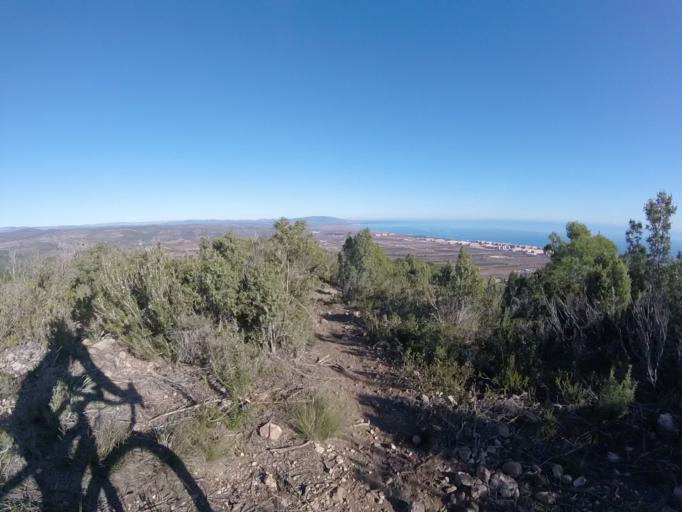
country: ES
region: Valencia
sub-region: Provincia de Castello
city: Orpesa/Oropesa del Mar
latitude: 40.1044
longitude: 0.1148
